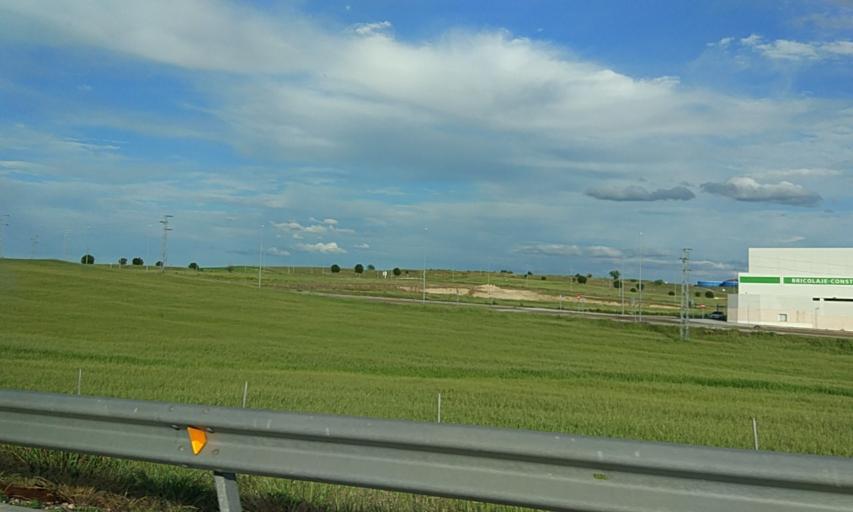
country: ES
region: Extremadura
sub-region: Provincia de Badajoz
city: Badajoz
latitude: 38.9034
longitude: -6.9988
